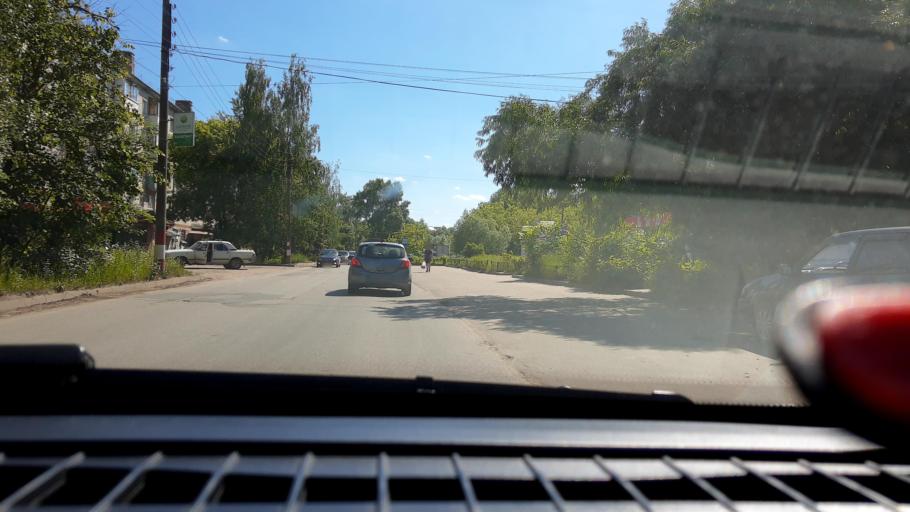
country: RU
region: Nizjnij Novgorod
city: Novaya Balakhna
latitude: 56.5215
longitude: 43.5654
